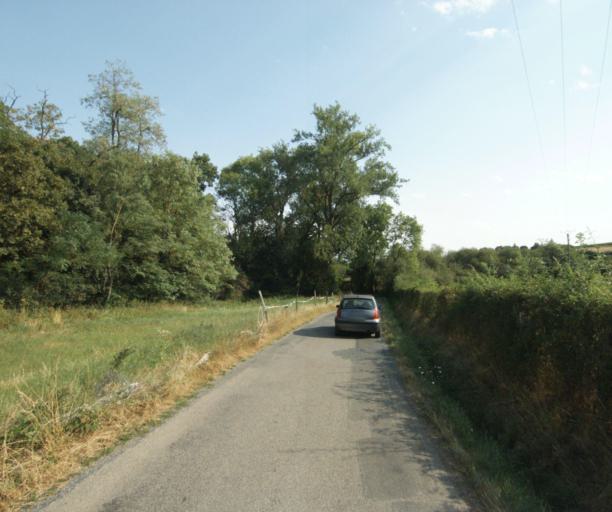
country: FR
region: Rhone-Alpes
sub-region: Departement du Rhone
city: Savigny
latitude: 45.8335
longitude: 4.5747
